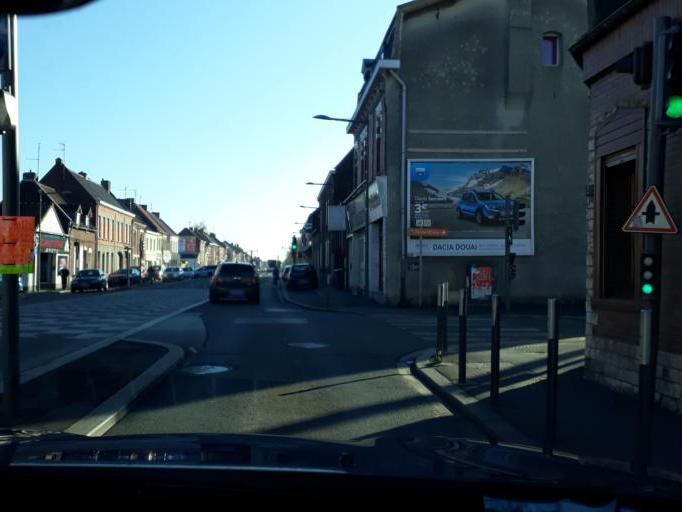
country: FR
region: Nord-Pas-de-Calais
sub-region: Departement du Nord
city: Sin-le-Noble
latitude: 50.3527
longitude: 3.1286
